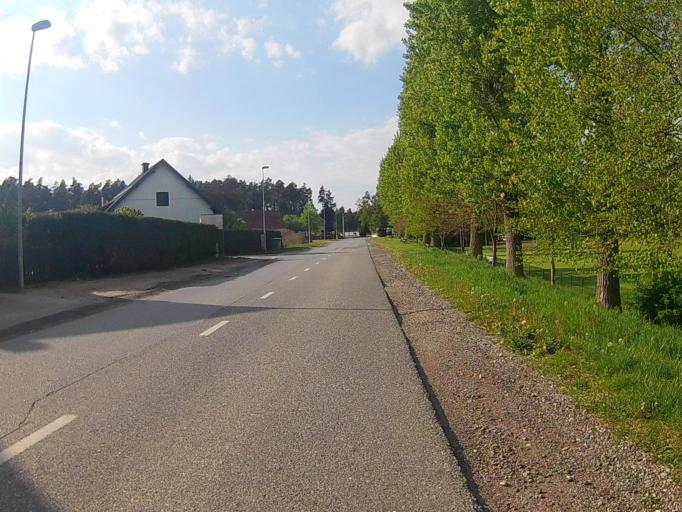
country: SI
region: Starse
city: Starse
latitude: 46.4554
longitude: 15.7307
